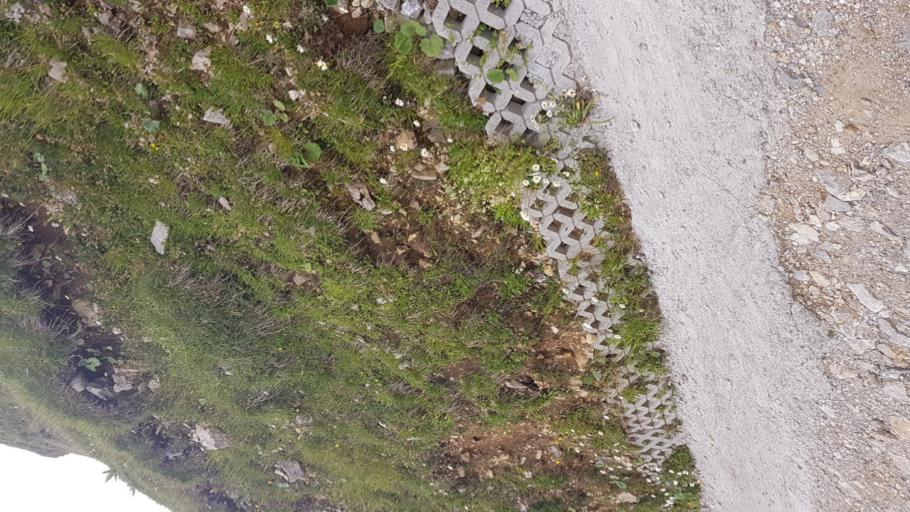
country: CH
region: Bern
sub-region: Obersimmental-Saanen District
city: Boltigen
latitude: 46.6956
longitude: 7.4435
